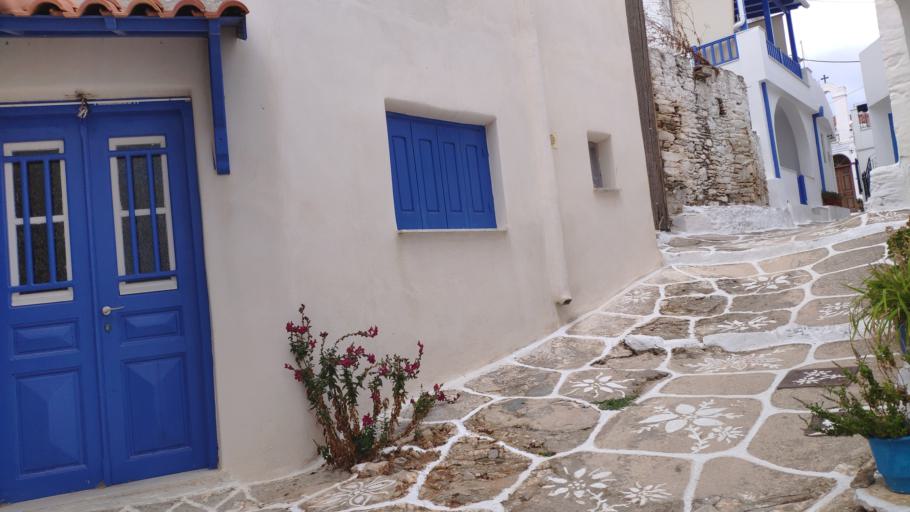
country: GR
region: South Aegean
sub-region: Nomos Kykladon
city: Kythnos
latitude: 37.4119
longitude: 24.4317
